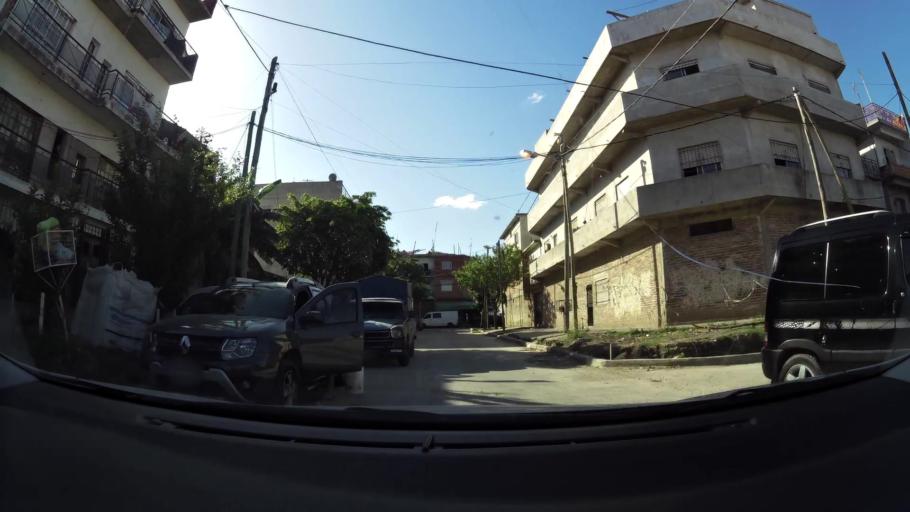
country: AR
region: Buenos Aires F.D.
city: Villa Lugano
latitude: -34.7007
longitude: -58.4845
